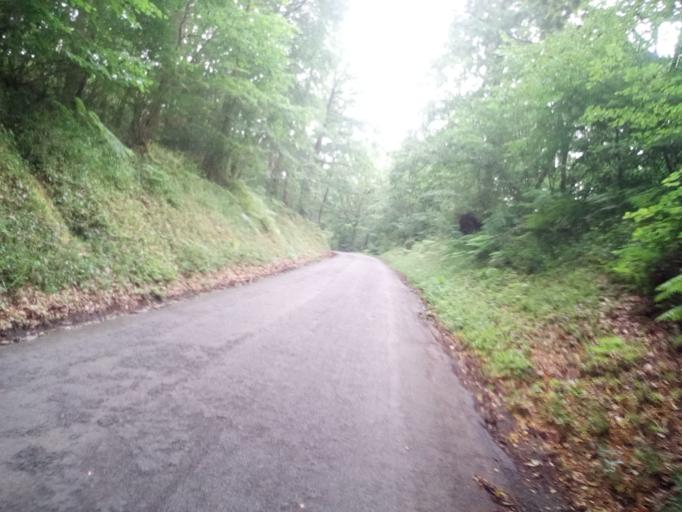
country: FR
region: Lower Normandy
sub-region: Departement du Calvados
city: Clinchamps-sur-Orne
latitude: 49.0493
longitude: -0.4382
